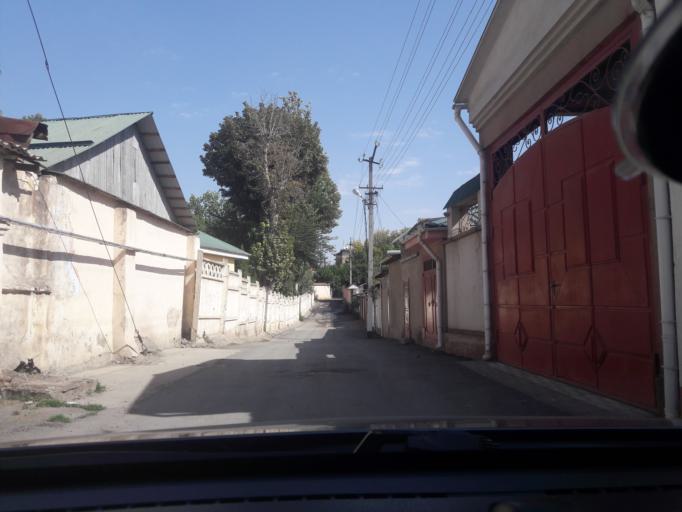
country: TJ
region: Dushanbe
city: Dushanbe
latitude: 38.5772
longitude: 68.7977
